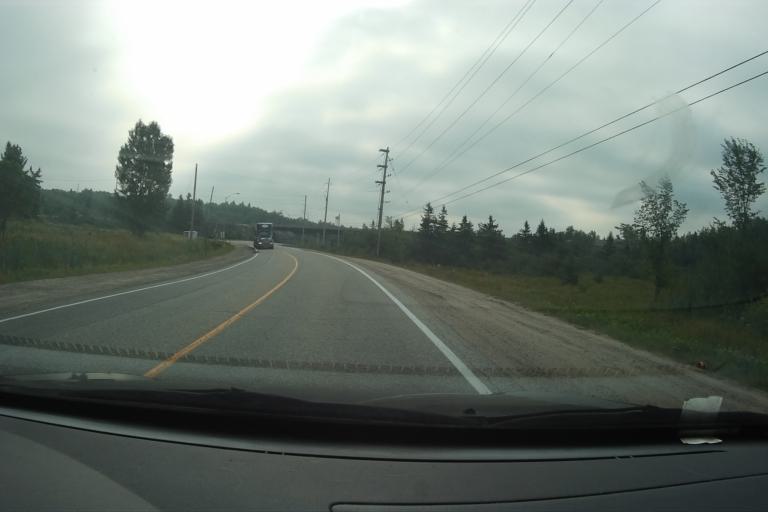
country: CA
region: Ontario
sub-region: Nipissing District
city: North Bay
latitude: 46.1972
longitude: -79.3593
